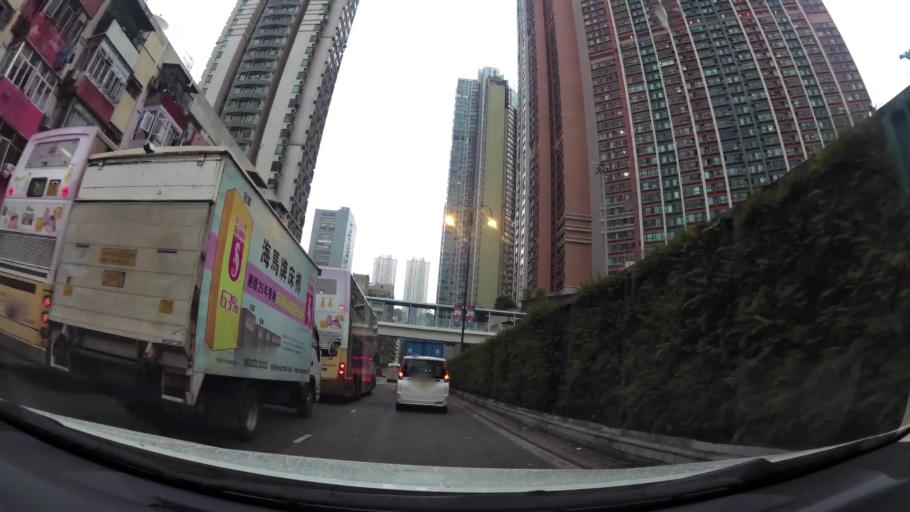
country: HK
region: Tsuen Wan
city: Tsuen Wan
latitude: 22.3678
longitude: 114.1162
